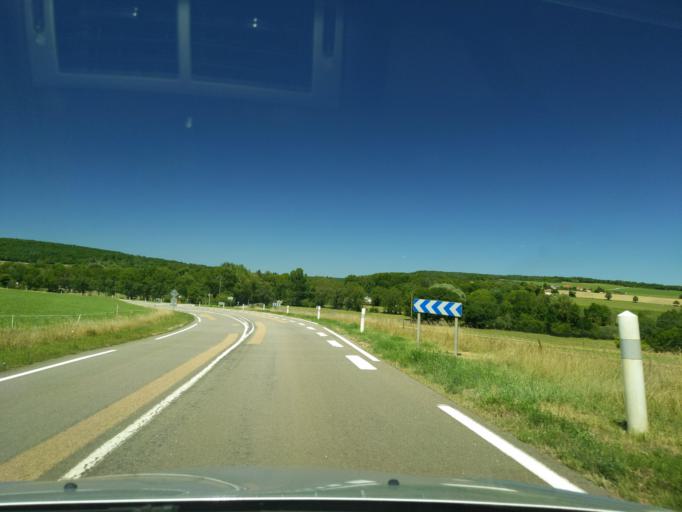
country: FR
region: Bourgogne
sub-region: Departement de la Cote-d'Or
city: Is-sur-Tille
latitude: 47.5141
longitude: 5.0731
